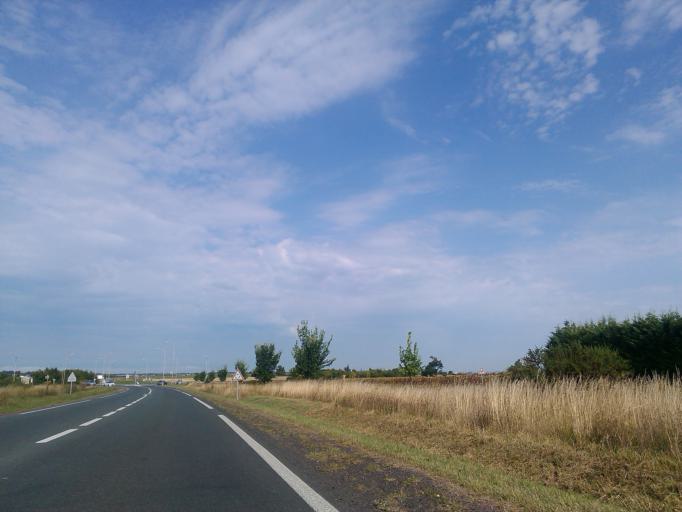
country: FR
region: Poitou-Charentes
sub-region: Departement de la Charente-Maritime
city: Etaules
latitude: 45.7404
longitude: -1.0898
